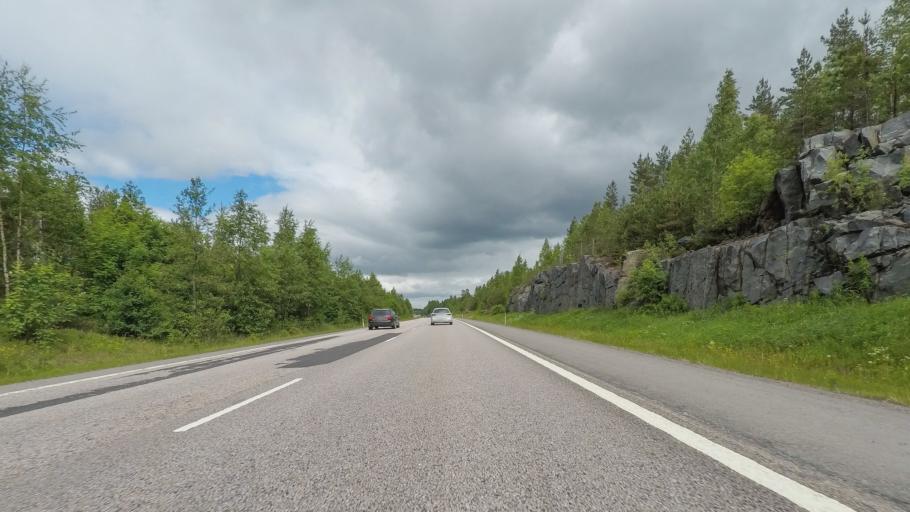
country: FI
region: Uusimaa
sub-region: Porvoo
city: Pukkila
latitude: 60.7833
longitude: 25.4842
